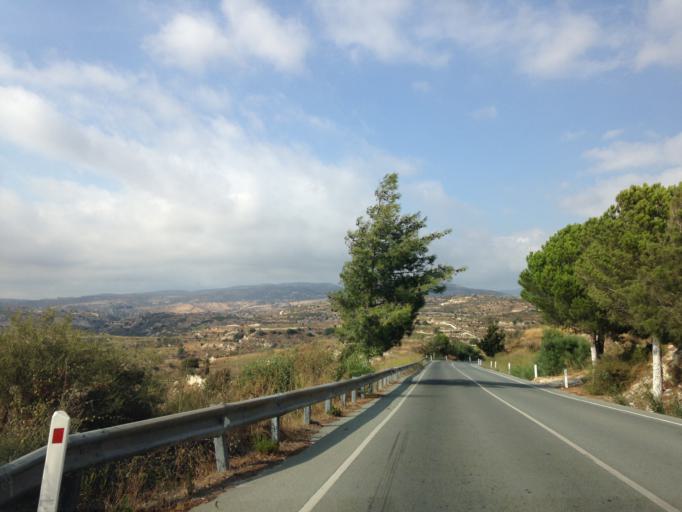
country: CY
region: Limassol
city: Pachna
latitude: 34.7903
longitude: 32.7991
